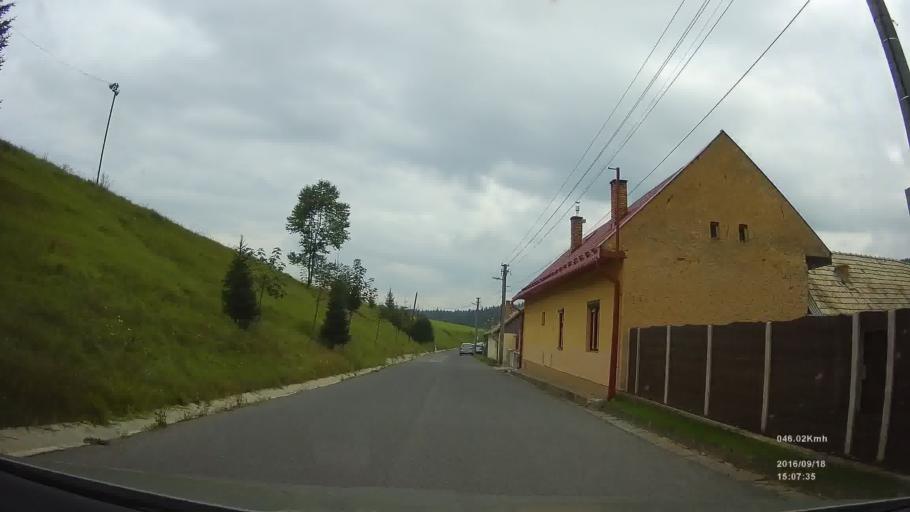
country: SK
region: Presovsky
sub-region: Okres Presov
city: Levoca
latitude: 49.0237
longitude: 20.5230
